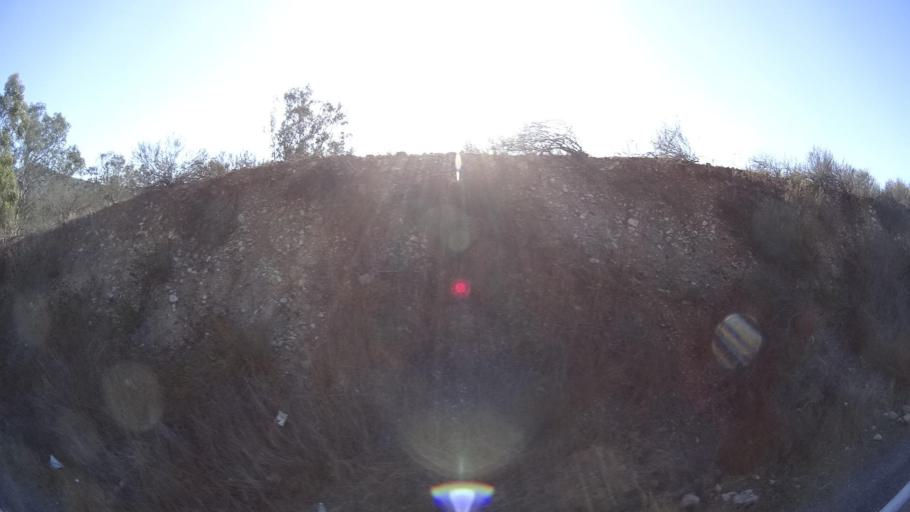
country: US
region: California
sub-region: San Diego County
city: La Presa
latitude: 32.6444
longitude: -116.9331
